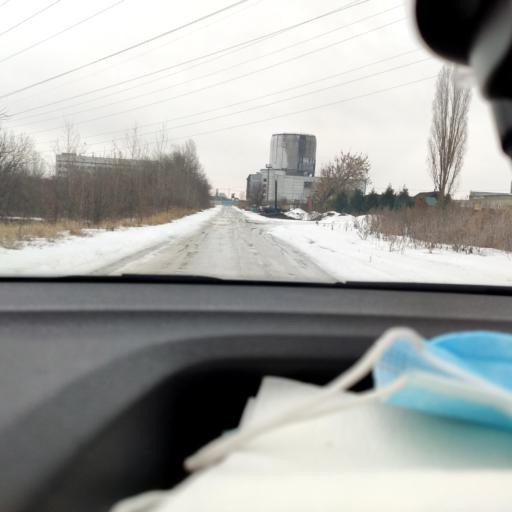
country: RU
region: Voronezj
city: Shilovo
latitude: 51.5639
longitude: 39.1433
